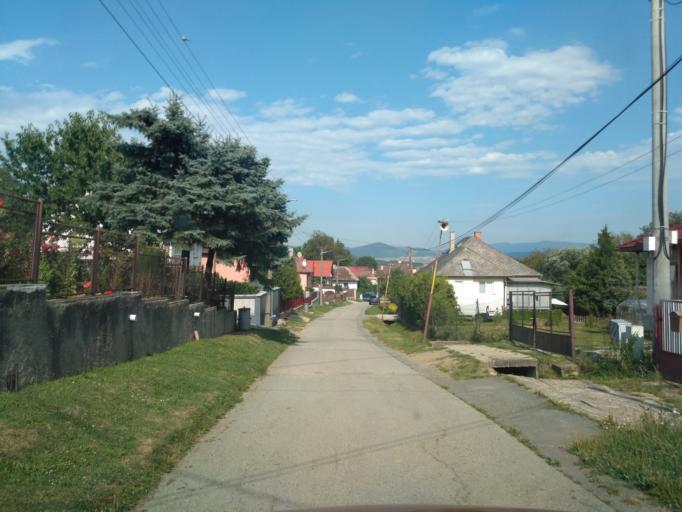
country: SK
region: Kosicky
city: Kosice
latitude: 48.8485
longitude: 21.2631
